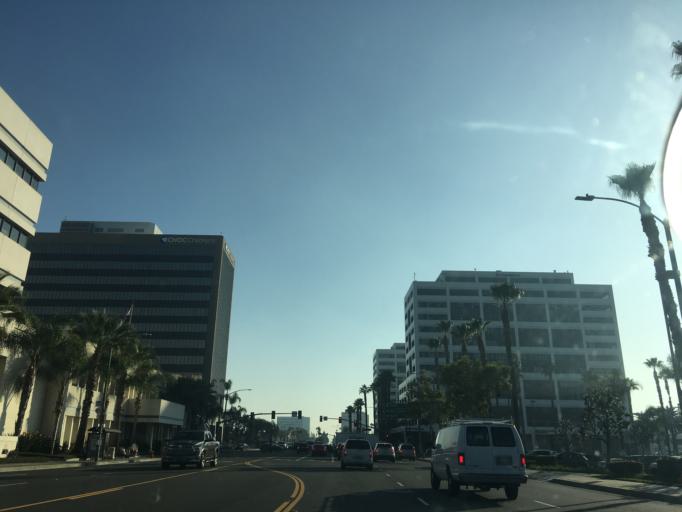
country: US
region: California
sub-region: Orange County
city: Orange
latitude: 33.7815
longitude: -117.8674
